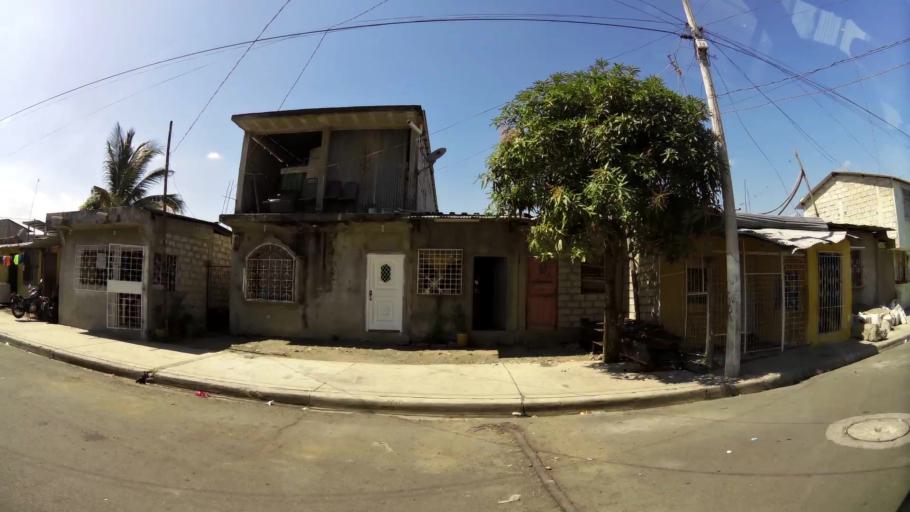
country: EC
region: Guayas
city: Guayaquil
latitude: -2.2266
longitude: -79.9326
